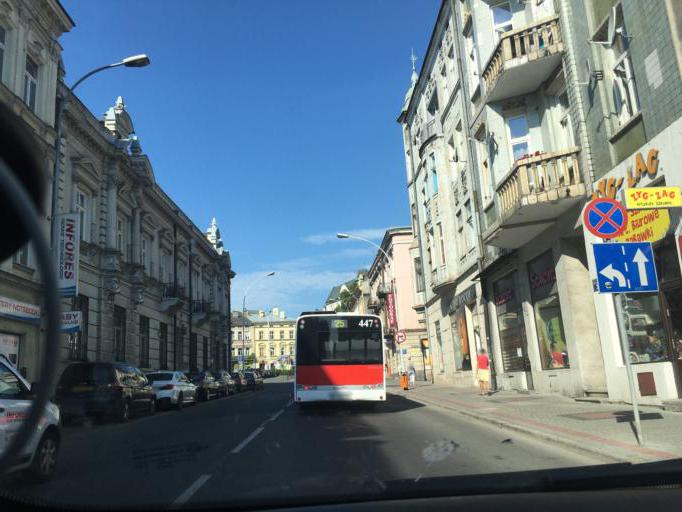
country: PL
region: Subcarpathian Voivodeship
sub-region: Przemysl
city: Przemysl
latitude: 49.7825
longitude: 22.7765
